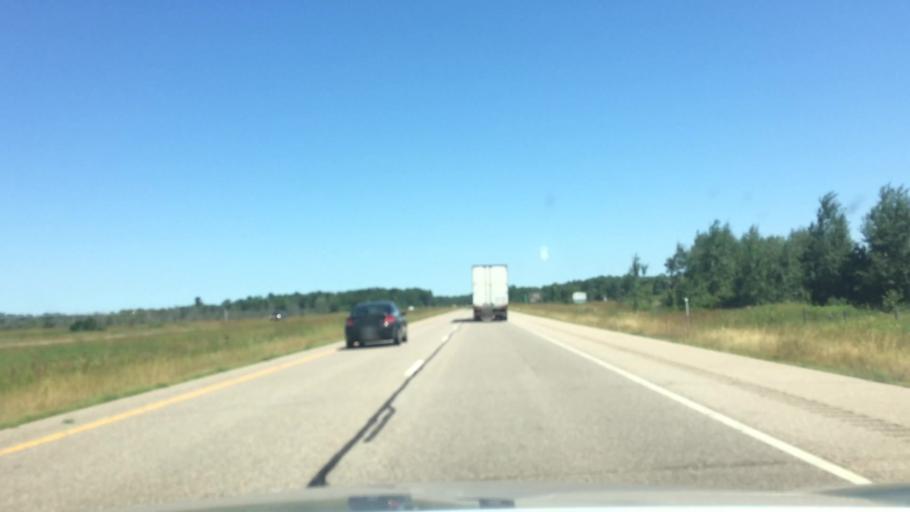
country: US
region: Wisconsin
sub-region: Waushara County
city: Wautoma
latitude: 44.1586
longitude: -89.5322
